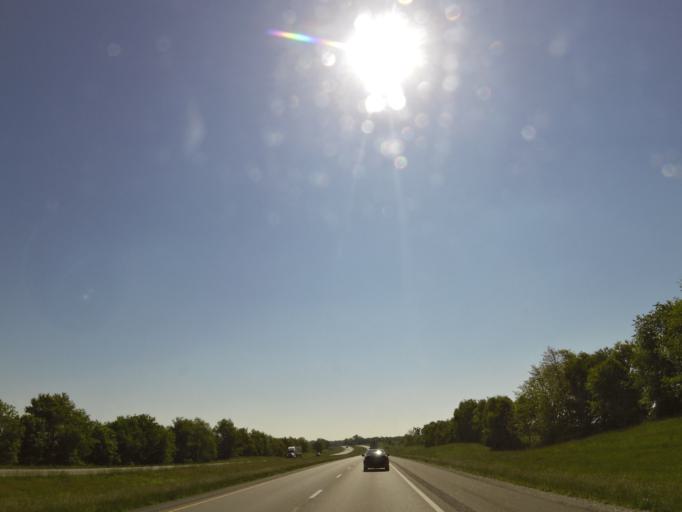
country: US
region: Kentucky
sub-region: Woodford County
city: Midway
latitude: 38.1593
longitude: -84.6670
